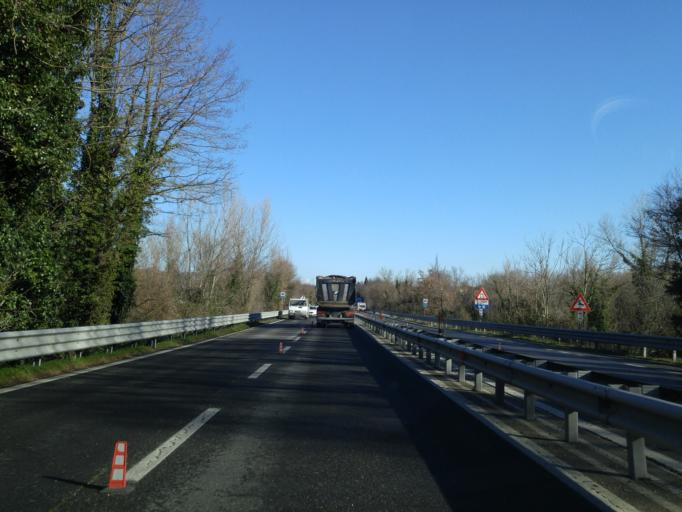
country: IT
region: The Marches
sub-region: Provincia di Pesaro e Urbino
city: Sant'Ippolito
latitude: 43.6944
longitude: 12.8605
